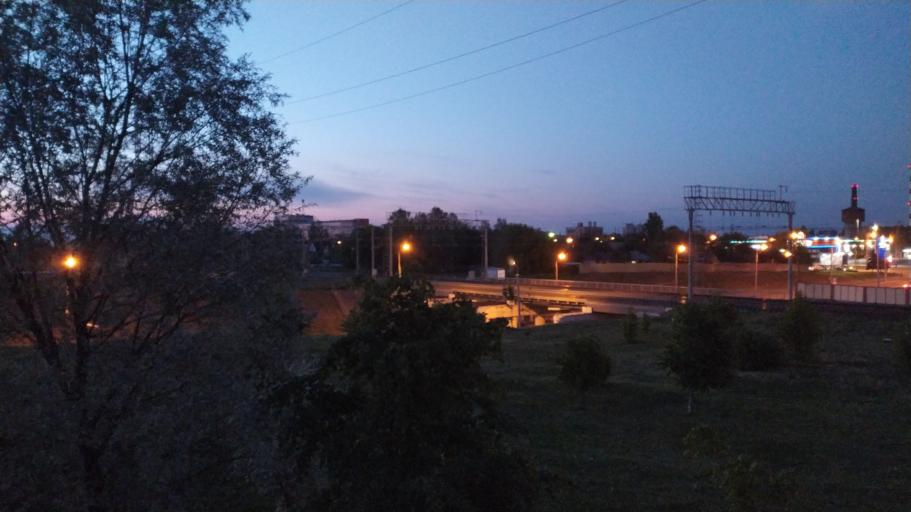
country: BY
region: Gomel
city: Gomel
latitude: 52.4672
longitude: 30.9782
